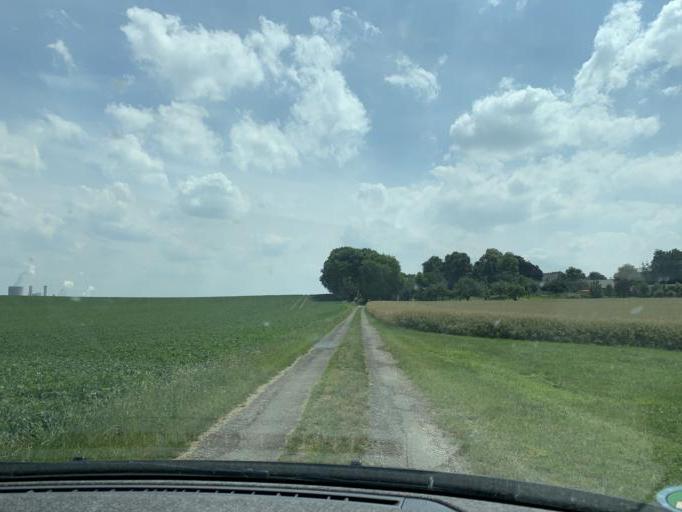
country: DE
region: North Rhine-Westphalia
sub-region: Regierungsbezirk Dusseldorf
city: Rommerskirchen
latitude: 51.0218
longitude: 6.6292
